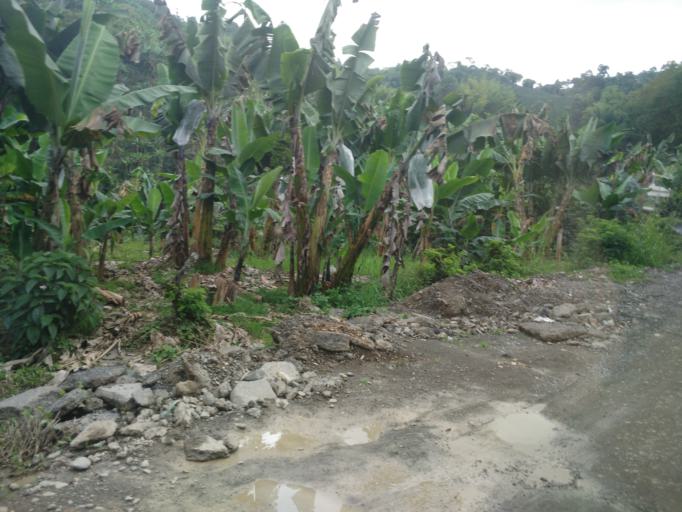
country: CO
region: Valle del Cauca
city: Sevilla
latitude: 4.2987
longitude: -75.8996
